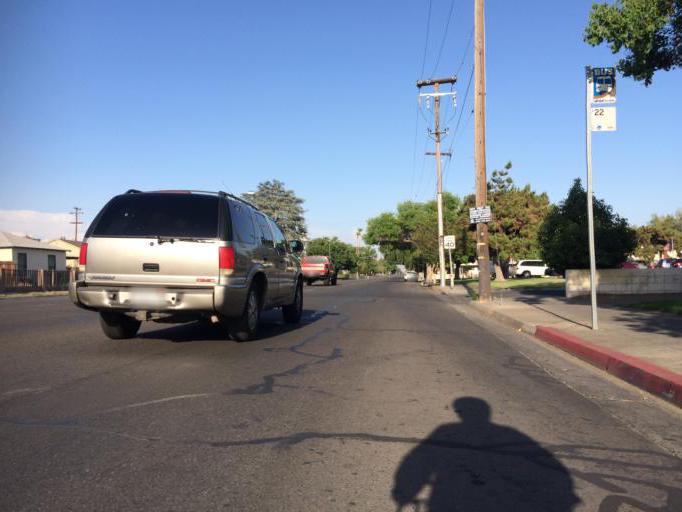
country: US
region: California
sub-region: Fresno County
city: Sunnyside
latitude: 36.7431
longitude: -119.7354
